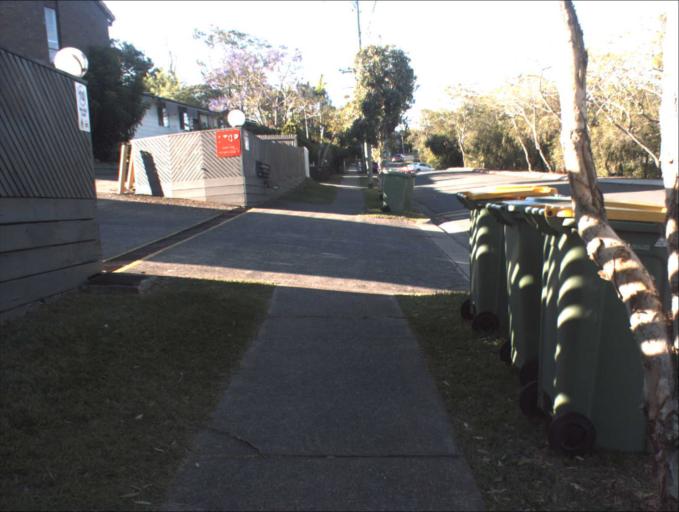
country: AU
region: Queensland
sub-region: Logan
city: Logan City
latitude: -27.6405
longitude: 153.1184
